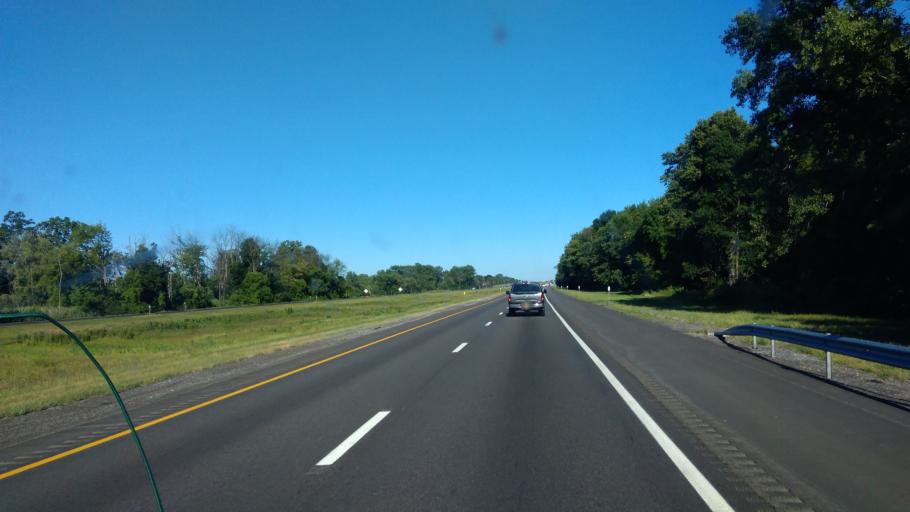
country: US
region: New York
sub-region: Ontario County
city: Clifton Springs
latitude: 42.9734
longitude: -77.1478
